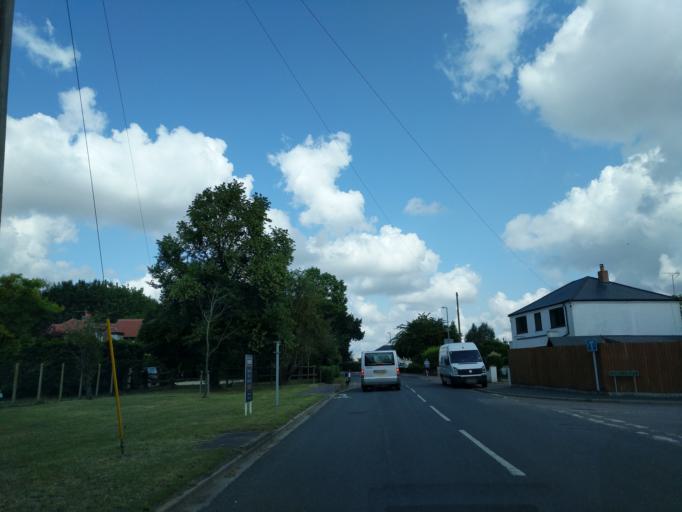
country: GB
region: England
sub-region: Suffolk
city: Exning
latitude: 52.3095
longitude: 0.3827
